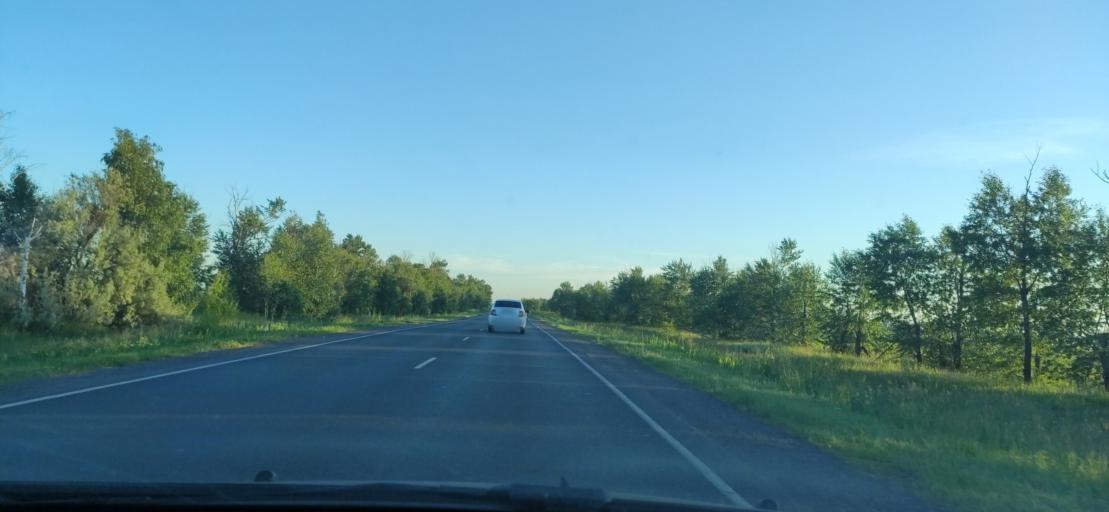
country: RU
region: Ulyanovsk
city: Cherdakly
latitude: 54.4018
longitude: 48.8634
